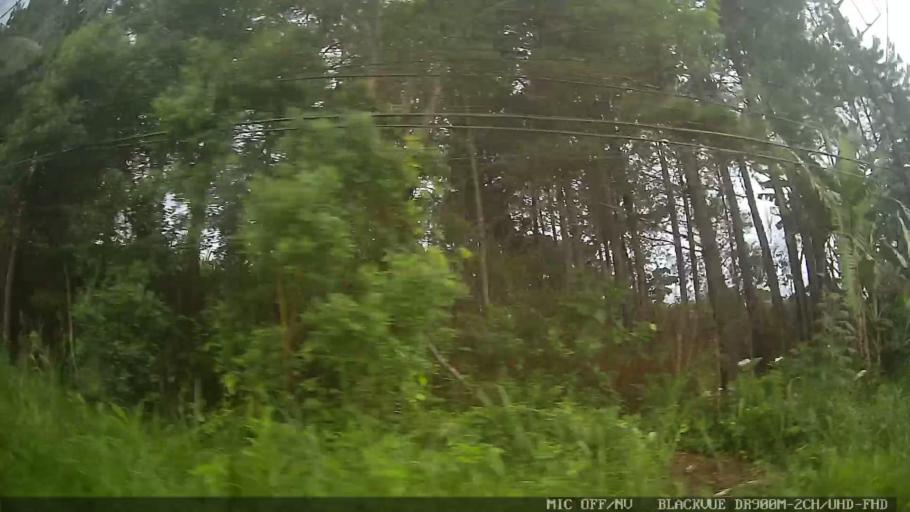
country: BR
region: Sao Paulo
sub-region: Ribeirao Pires
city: Ribeirao Pires
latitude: -23.6901
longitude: -46.3527
